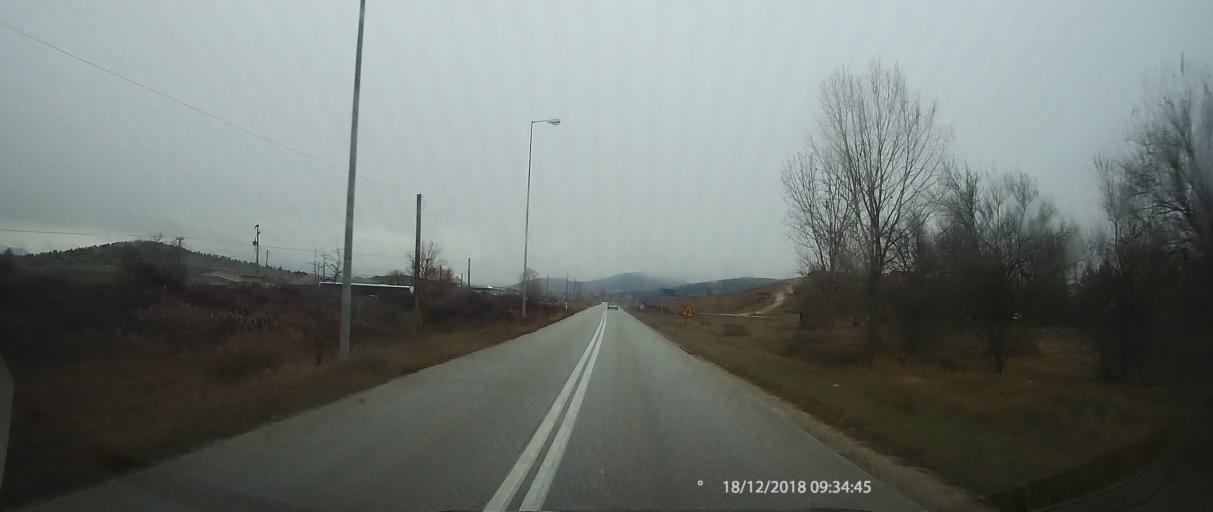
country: GR
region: Thessaly
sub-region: Nomos Larisis
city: Elassona
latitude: 39.9769
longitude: 22.1843
